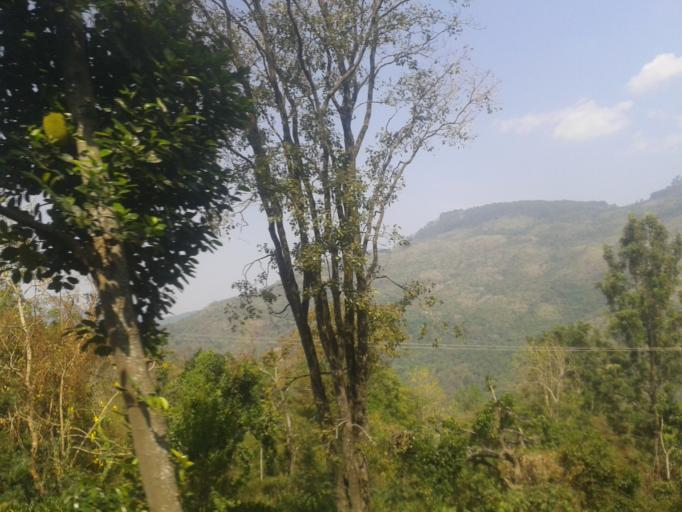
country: IN
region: Tamil Nadu
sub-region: Dindigul
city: Ayakudi
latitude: 10.3520
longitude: 77.5752
